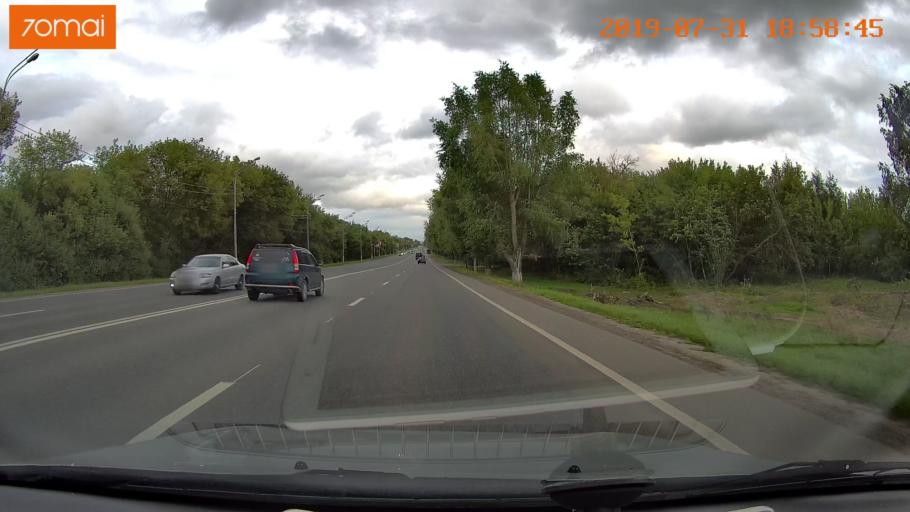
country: RU
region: Moskovskaya
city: Raduzhnyy
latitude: 55.1444
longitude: 38.7080
